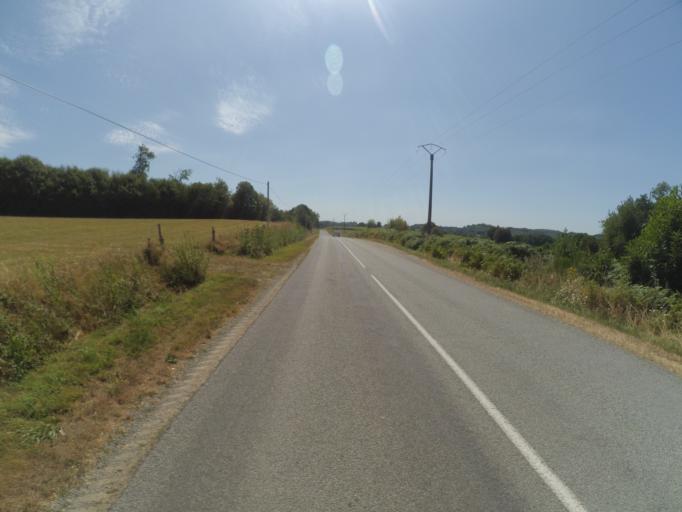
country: FR
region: Limousin
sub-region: Departement de la Creuse
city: Le Grand-Bourg
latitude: 46.1385
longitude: 1.6639
